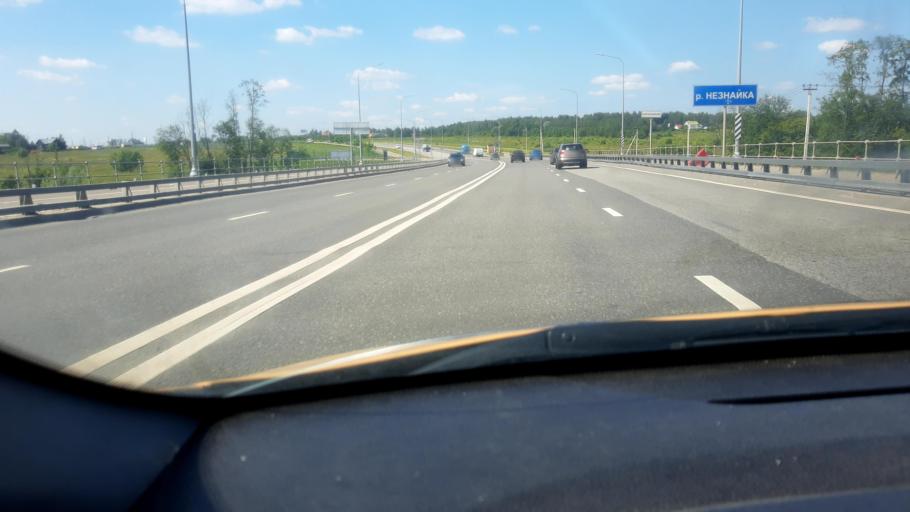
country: RU
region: Moskovskaya
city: Kokoshkino
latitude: 55.5830
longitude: 37.1640
